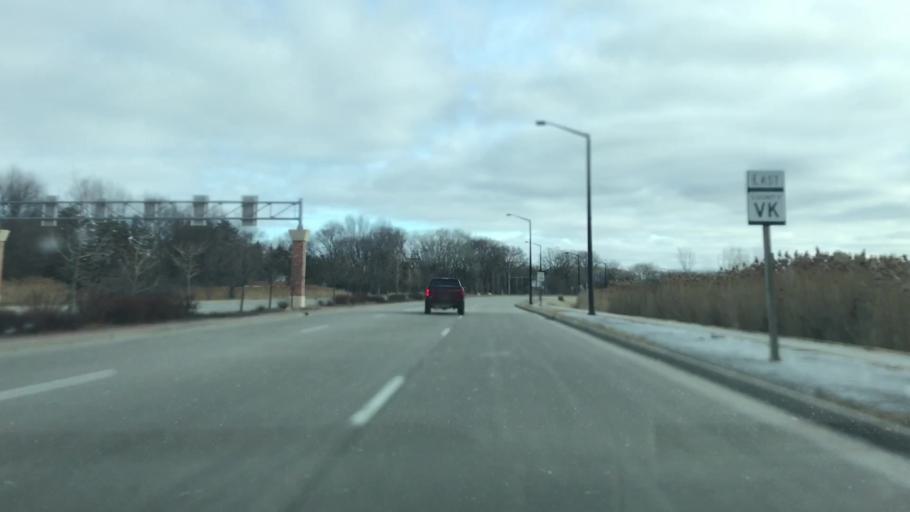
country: US
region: Wisconsin
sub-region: Brown County
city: Ashwaubenon
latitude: 44.5090
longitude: -88.0807
